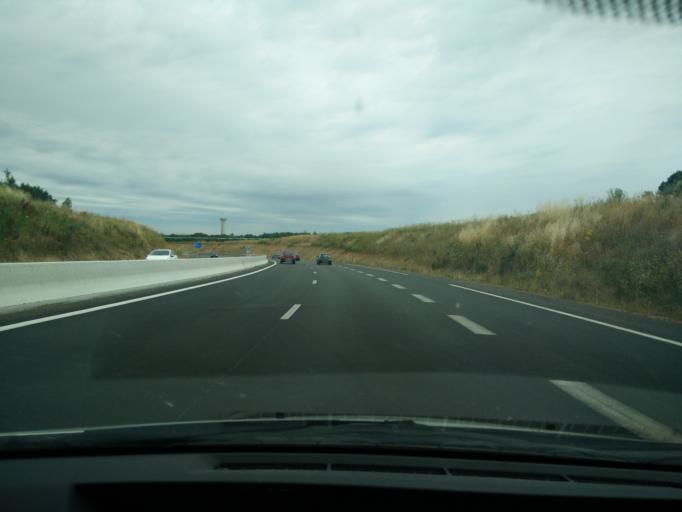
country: FR
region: Pays de la Loire
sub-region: Departement de Maine-et-Loire
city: Saint-Melaine-sur-Aubance
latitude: 47.3944
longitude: -0.5040
